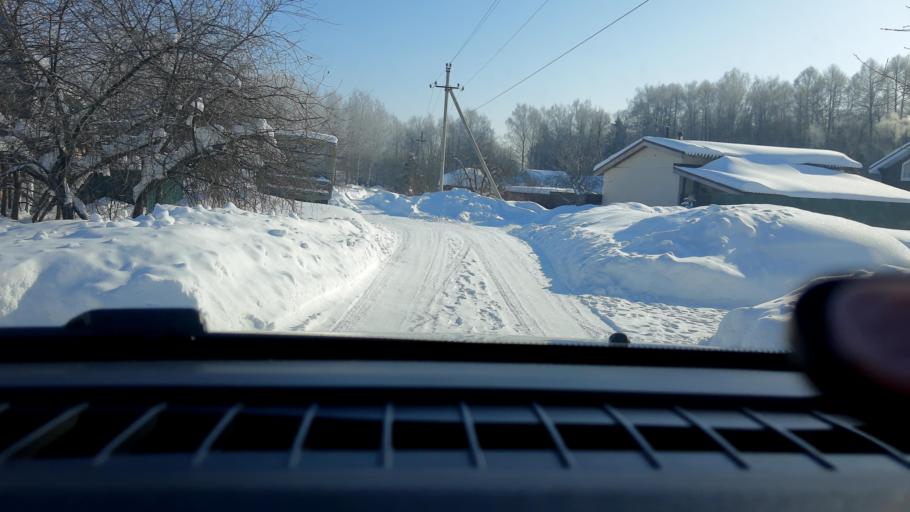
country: RU
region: Nizjnij Novgorod
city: Afonino
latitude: 56.1980
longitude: 44.0406
